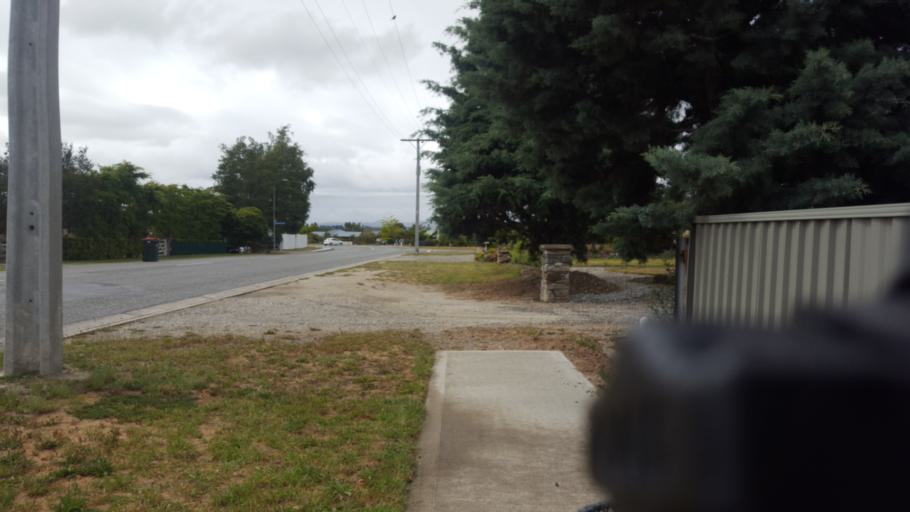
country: NZ
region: Otago
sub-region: Queenstown-Lakes District
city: Wanaka
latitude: -45.1919
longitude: 169.3292
